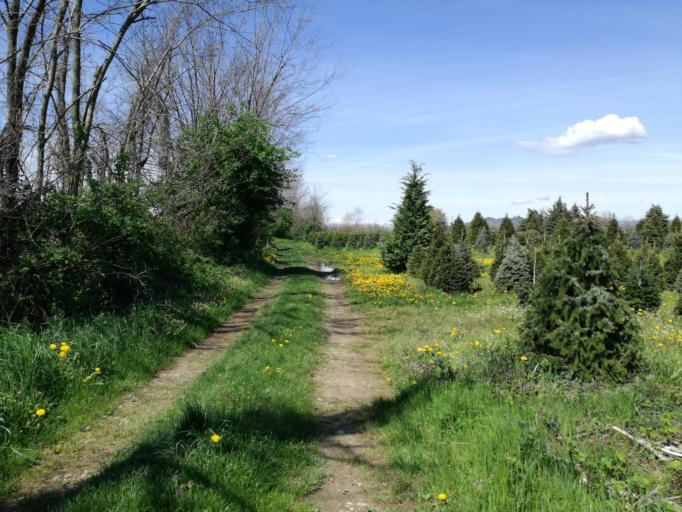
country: IT
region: Lombardy
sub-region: Provincia di Lecco
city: Verderio Superiore
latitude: 45.6742
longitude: 9.4348
